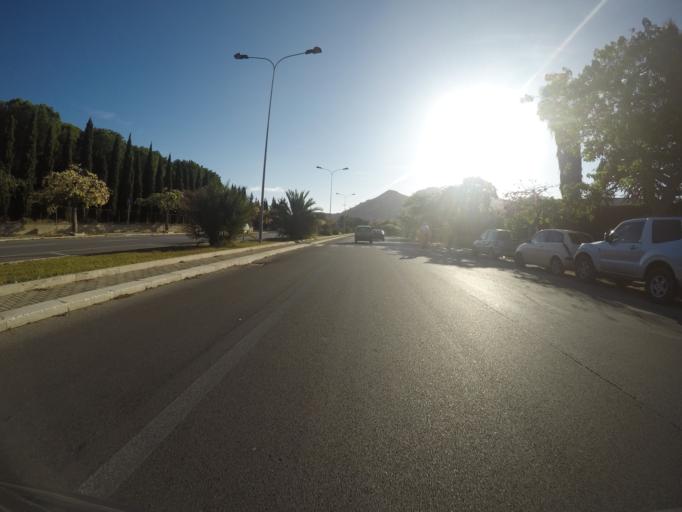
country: IT
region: Sicily
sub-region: Palermo
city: Palermo
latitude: 38.1889
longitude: 13.3123
